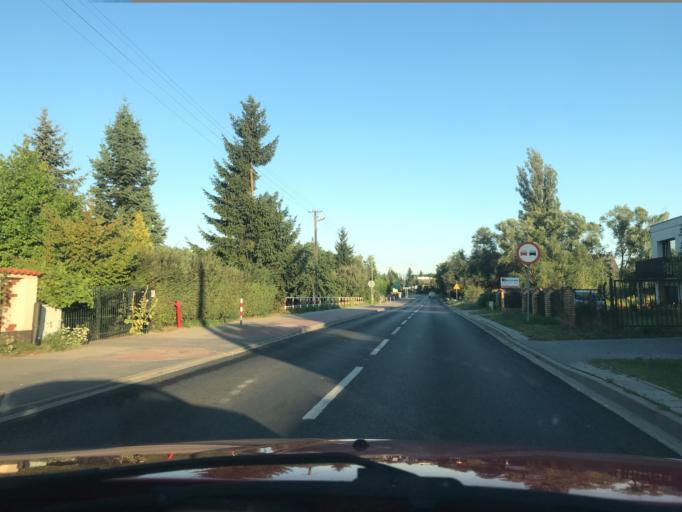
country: PL
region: Greater Poland Voivodeship
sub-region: Powiat poznanski
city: Tarnowo Podgorne
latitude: 52.4259
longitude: 16.7153
